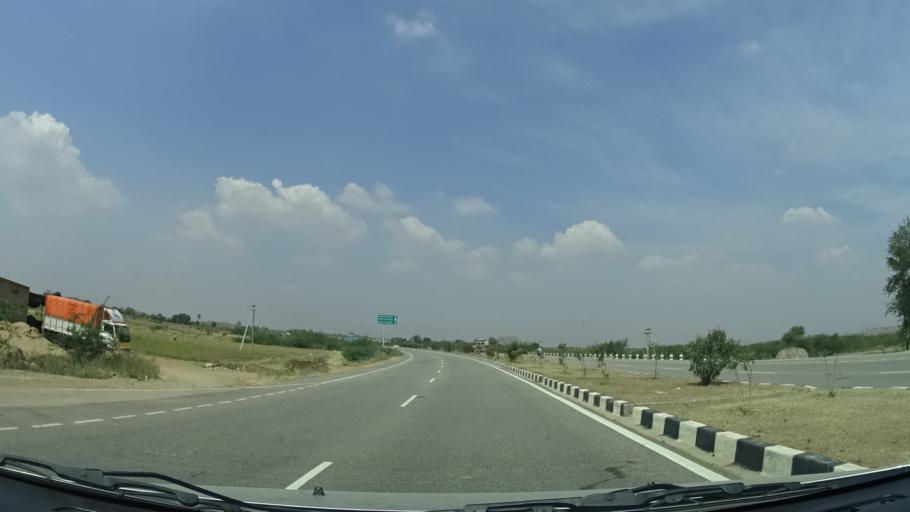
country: IN
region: Andhra Pradesh
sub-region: Anantapur
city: Dharmavaram
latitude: 14.4906
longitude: 77.6317
